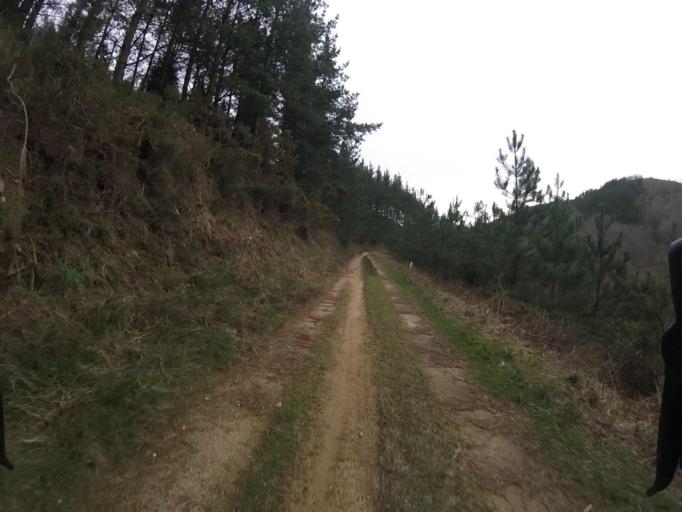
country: ES
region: Navarre
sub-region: Provincia de Navarra
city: Bera
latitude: 43.2902
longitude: -1.7342
